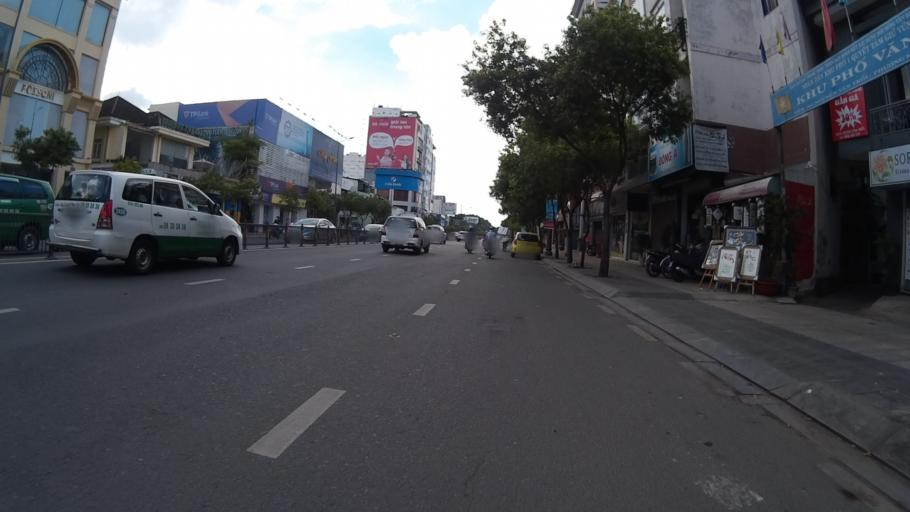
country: VN
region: Ho Chi Minh City
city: Quan Phu Nhuan
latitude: 10.7987
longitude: 106.6702
